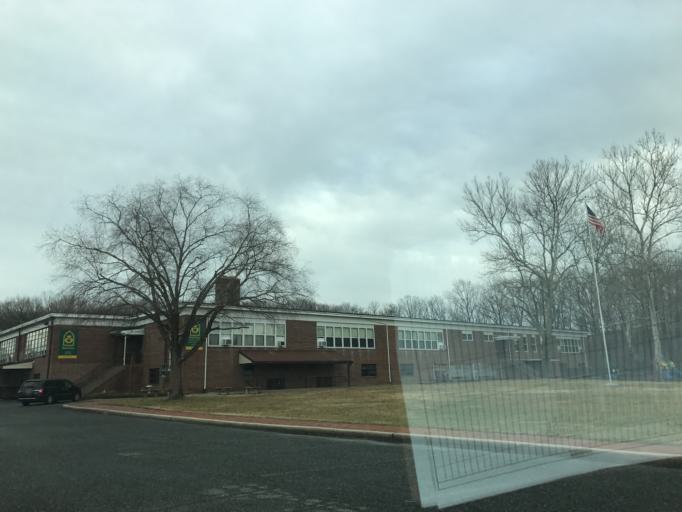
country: US
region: Maryland
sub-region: Baltimore County
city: Essex
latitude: 39.3161
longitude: -76.4700
